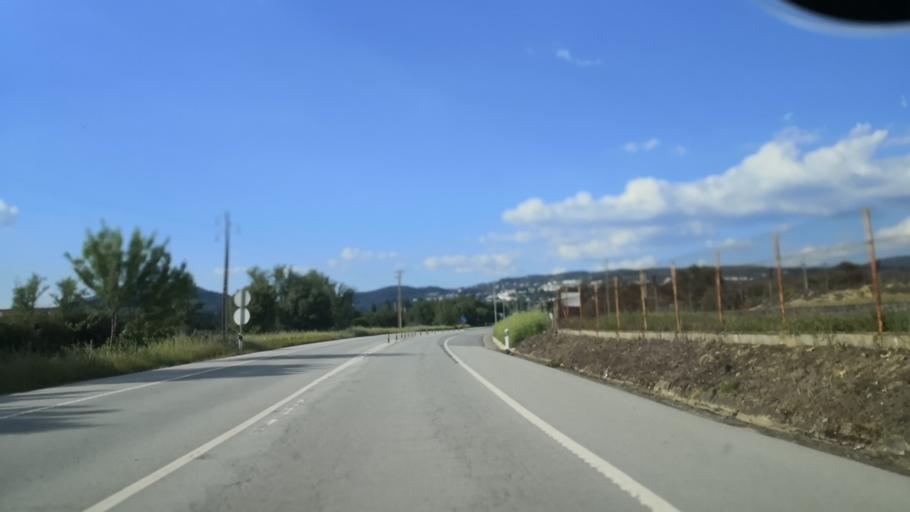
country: PT
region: Portalegre
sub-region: Portalegre
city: Portalegre
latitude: 39.2609
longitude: -7.4453
